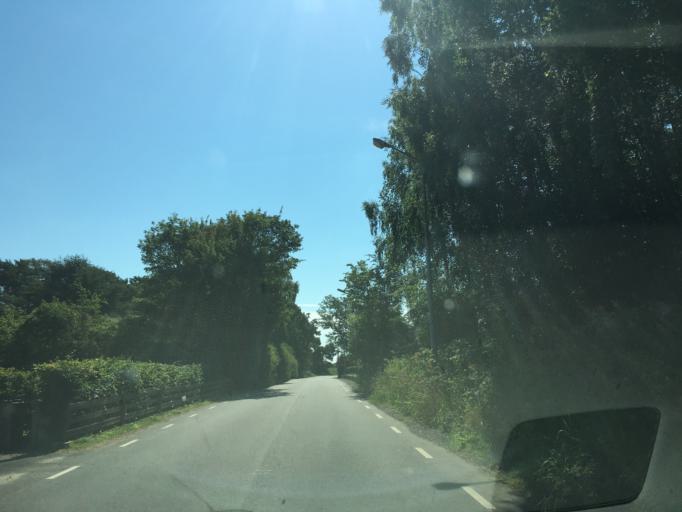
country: SE
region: Skane
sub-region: Simrishamns Kommun
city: Simrishamn
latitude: 55.5954
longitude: 14.3081
